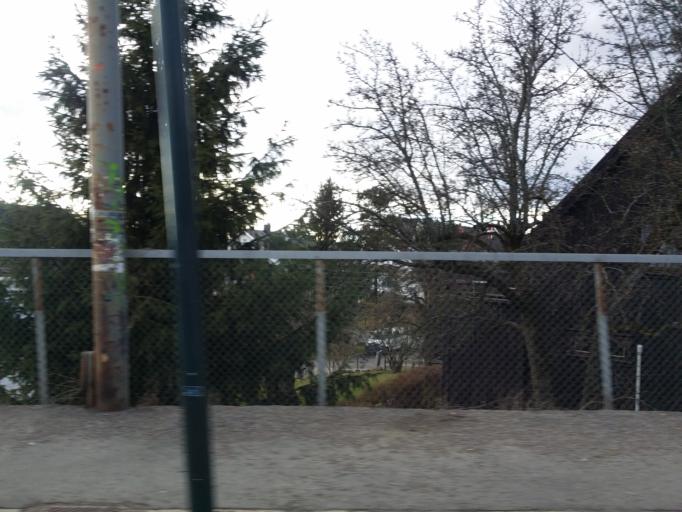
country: NO
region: Oslo
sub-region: Oslo
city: Oslo
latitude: 59.9497
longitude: 10.7901
